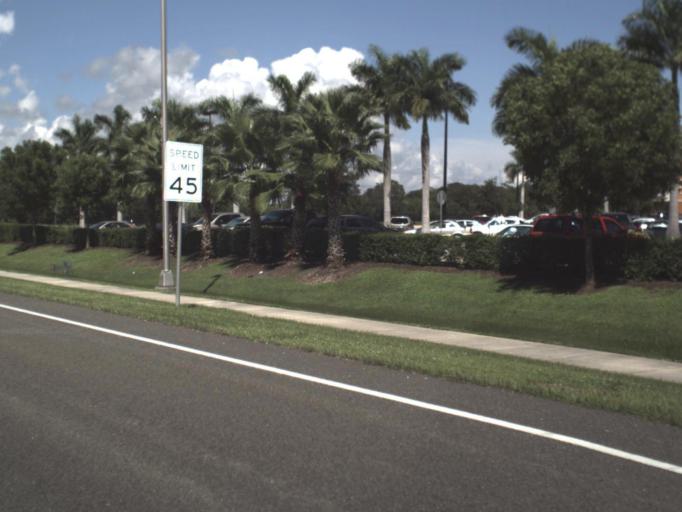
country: US
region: Florida
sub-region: Sarasota County
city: North Port
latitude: 27.0367
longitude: -82.2150
